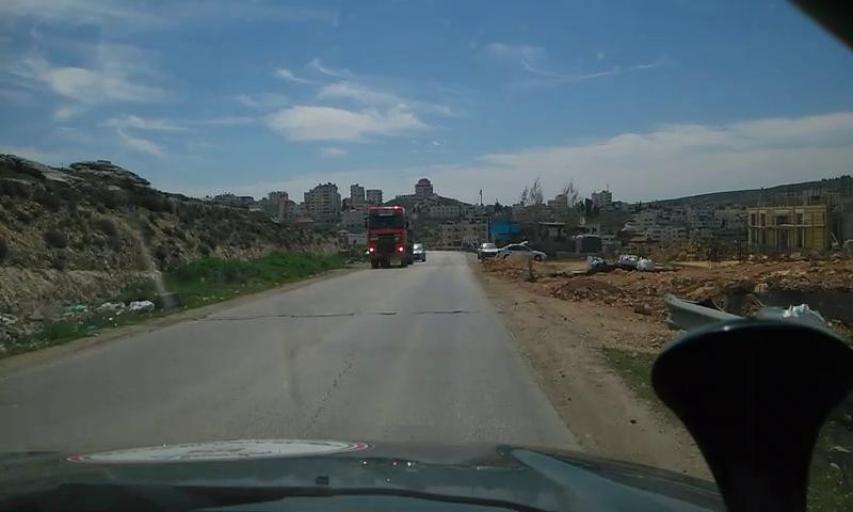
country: PS
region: West Bank
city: Al Judayrah
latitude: 31.8557
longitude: 35.2016
